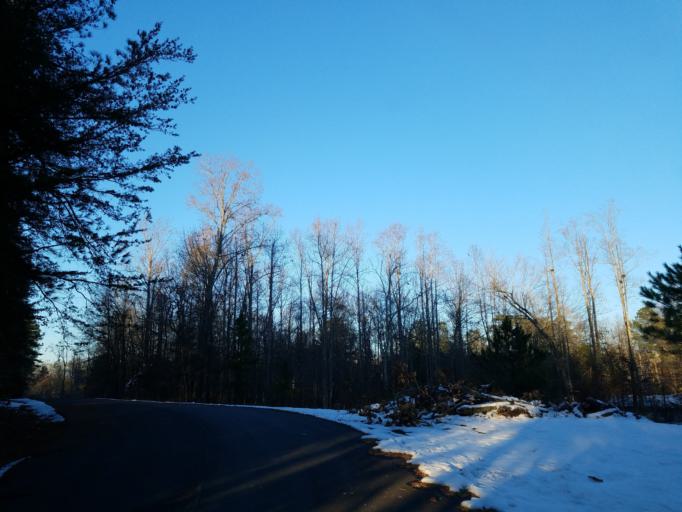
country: US
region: Georgia
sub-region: Dawson County
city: Dawsonville
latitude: 34.4233
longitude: -84.1168
